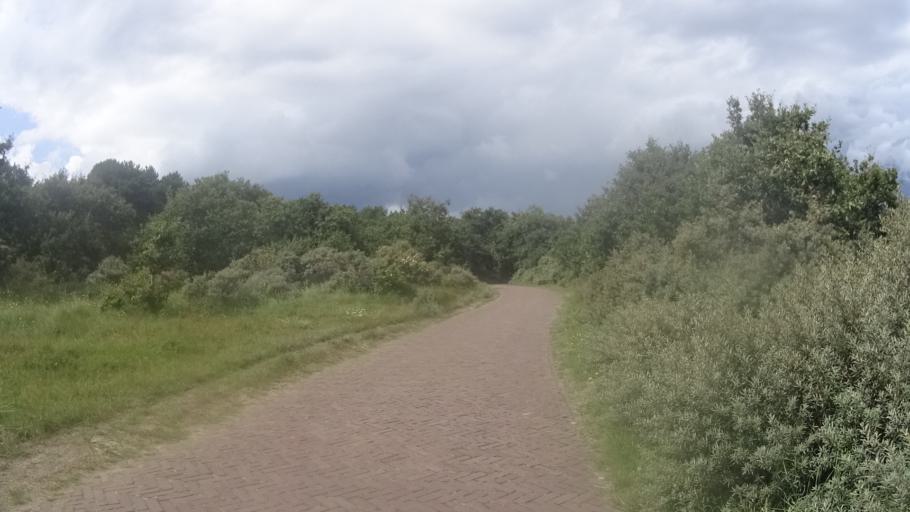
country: NL
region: North Holland
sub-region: Gemeente Bergen
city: Egmond aan Zee
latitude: 52.5917
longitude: 4.6383
